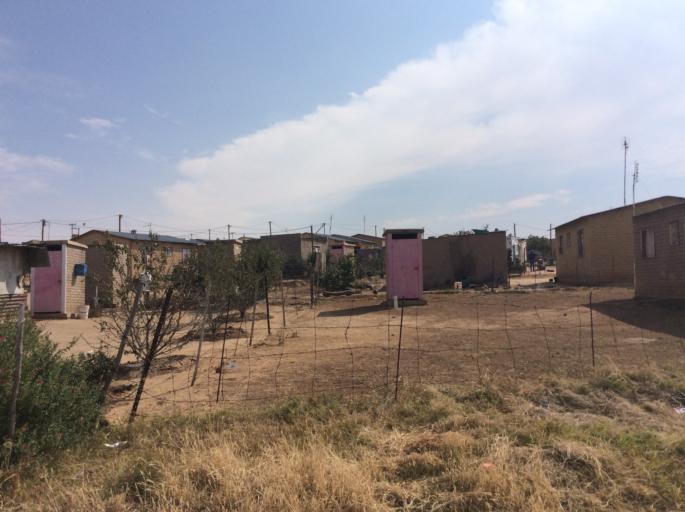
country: ZA
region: Orange Free State
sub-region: Xhariep District Municipality
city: Dewetsdorp
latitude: -29.5975
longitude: 26.6815
